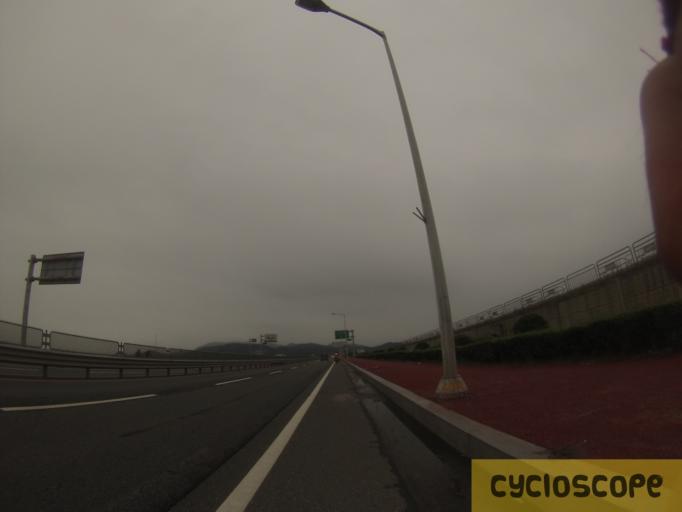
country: KR
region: Chungcheongnam-do
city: Taisen-ri
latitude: 36.1413
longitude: 126.5599
